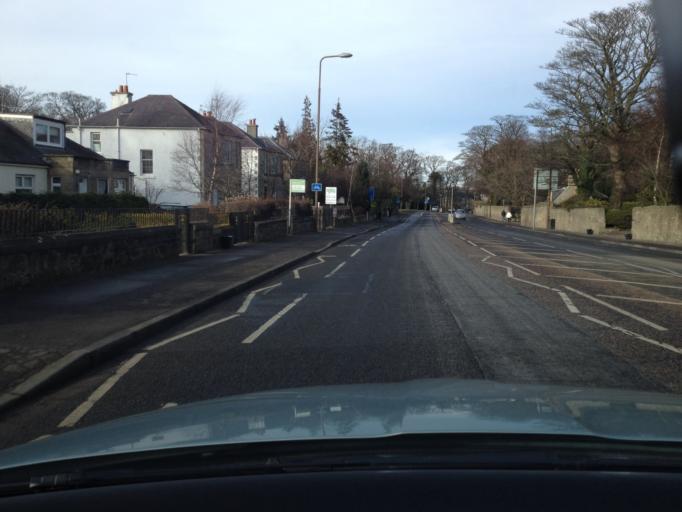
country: GB
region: Scotland
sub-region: Midlothian
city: Loanhead
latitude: 55.9014
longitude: -3.1644
